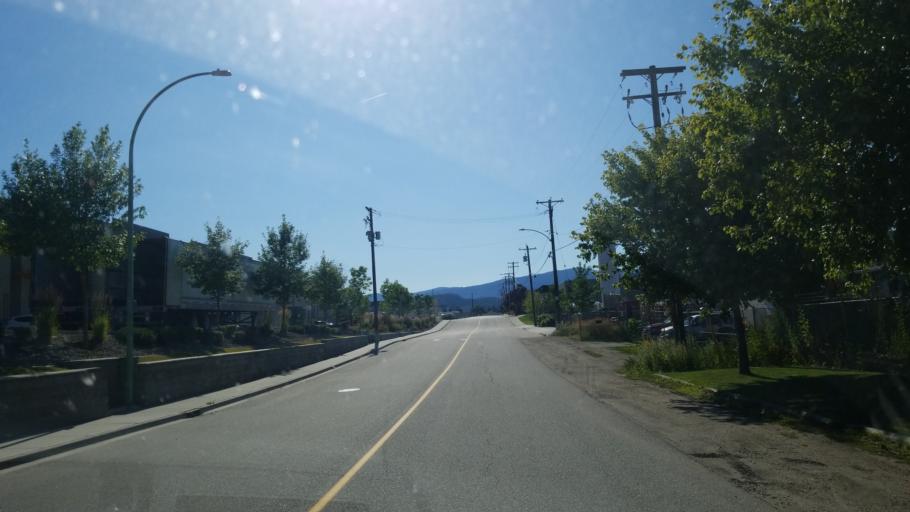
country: CA
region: British Columbia
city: Kelowna
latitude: 49.9220
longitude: -119.3815
